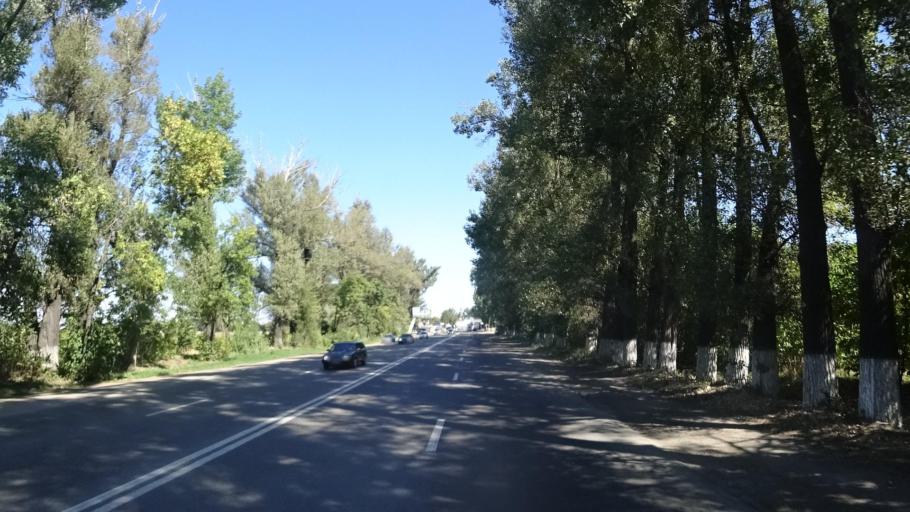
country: KZ
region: Almaty Oblysy
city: Energeticheskiy
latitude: 43.3345
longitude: 77.0382
